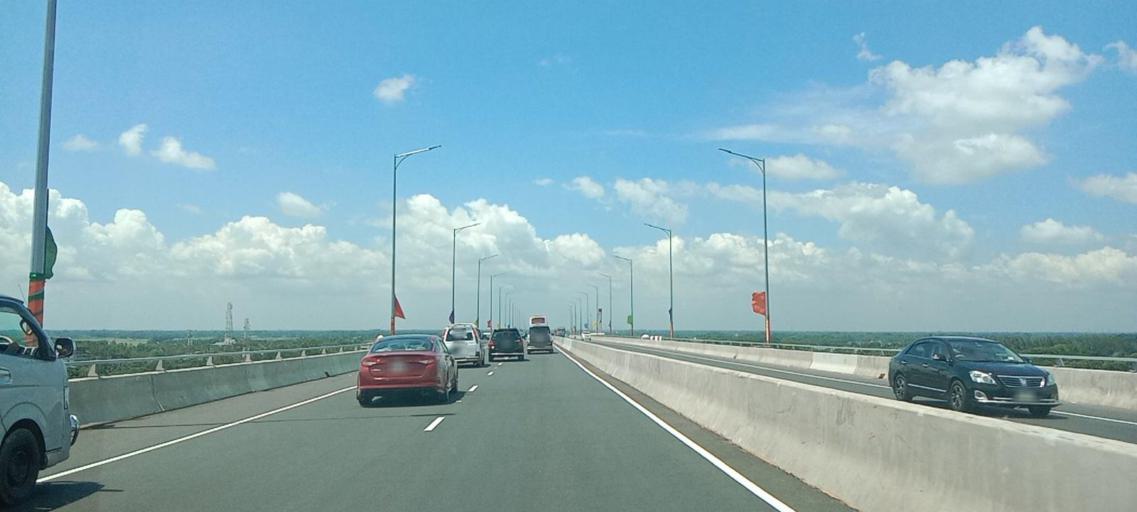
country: BD
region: Dhaka
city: Char Bhadrasan
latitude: 23.4677
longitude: 90.2639
